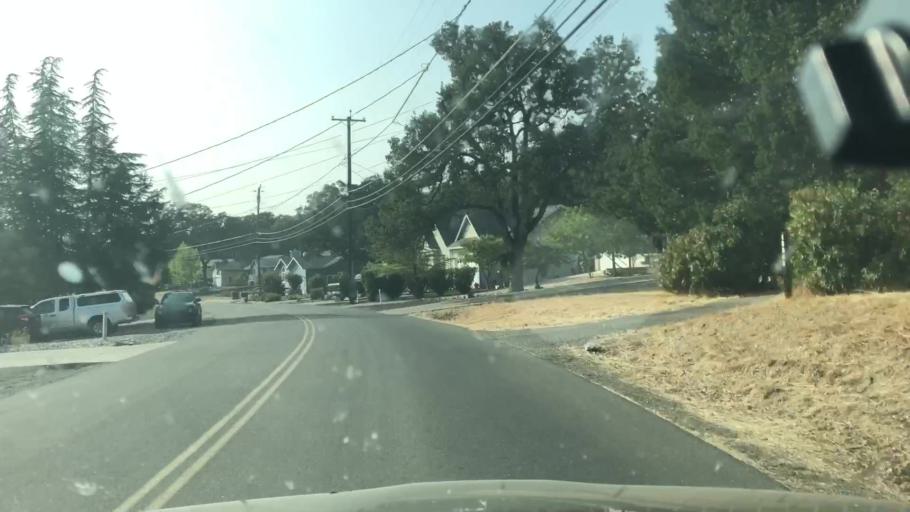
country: US
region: California
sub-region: Lake County
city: Hidden Valley Lake
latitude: 38.8019
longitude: -122.5574
